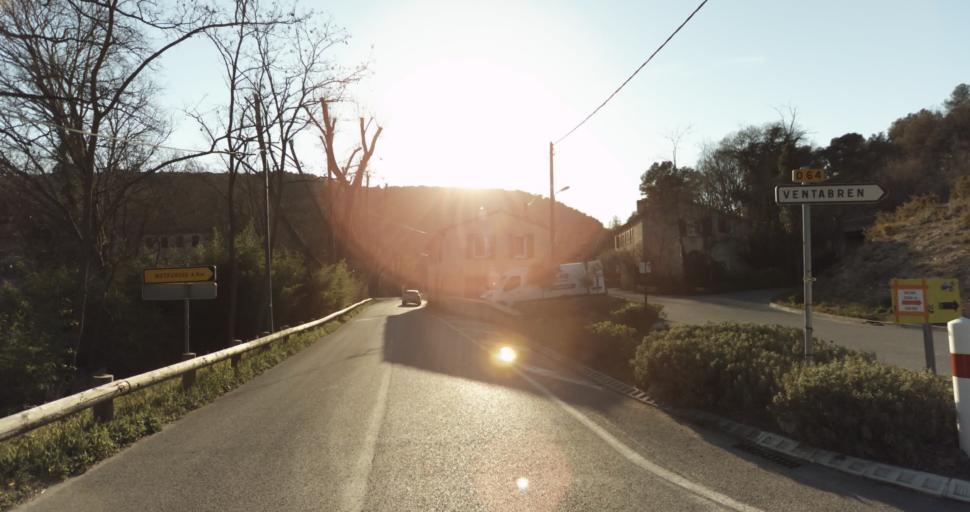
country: FR
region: Provence-Alpes-Cote d'Azur
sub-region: Departement des Bouches-du-Rhone
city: Ventabren
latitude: 43.5157
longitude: 5.3079
